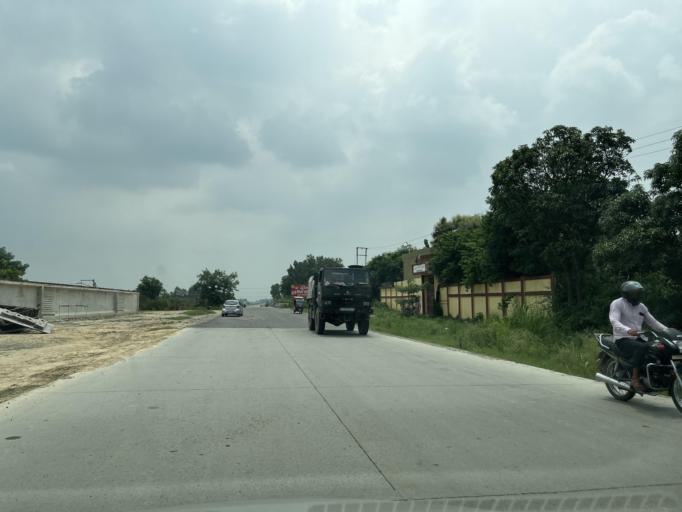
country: IN
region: Uttar Pradesh
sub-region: Bijnor
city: Najibabad
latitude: 29.5738
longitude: 78.3386
